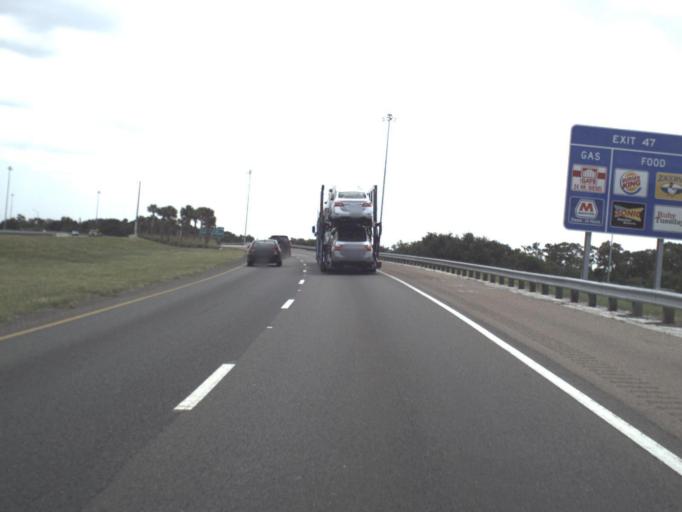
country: US
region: Florida
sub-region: Duval County
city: Jacksonville
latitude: 30.3543
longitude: -81.5555
